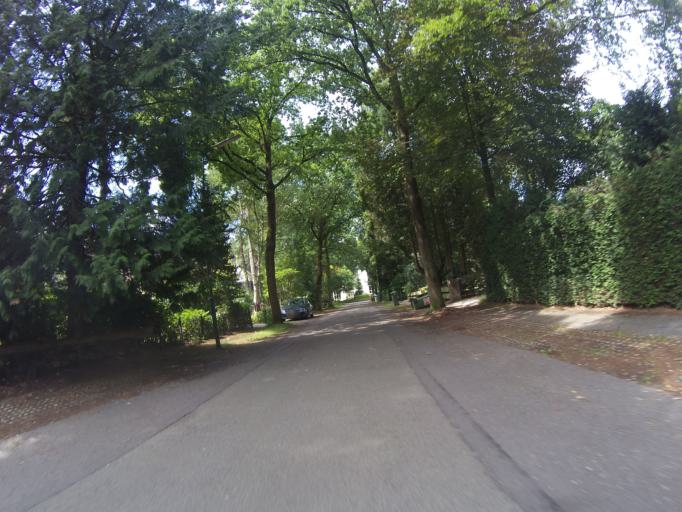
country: NL
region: Utrecht
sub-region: Gemeente Soest
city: Soest
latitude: 52.1582
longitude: 5.3111
